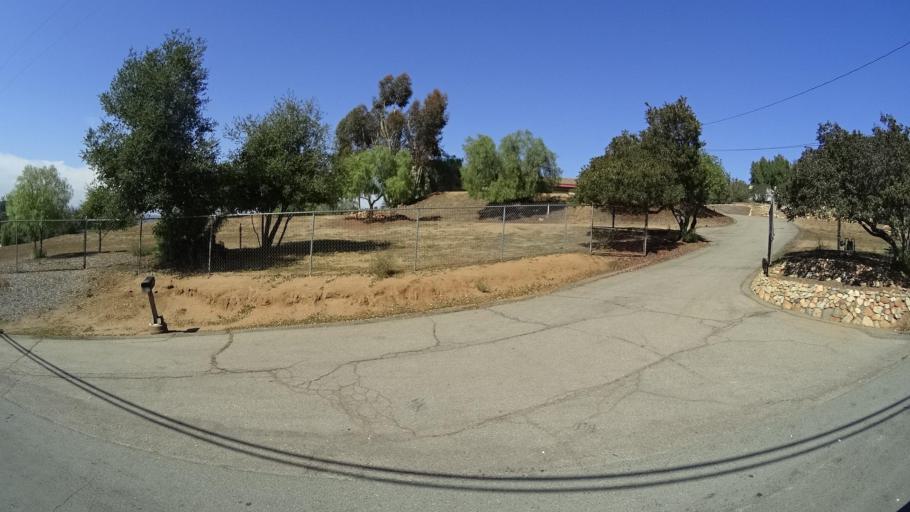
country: US
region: California
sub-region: San Diego County
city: Rancho San Diego
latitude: 32.7748
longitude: -116.9367
